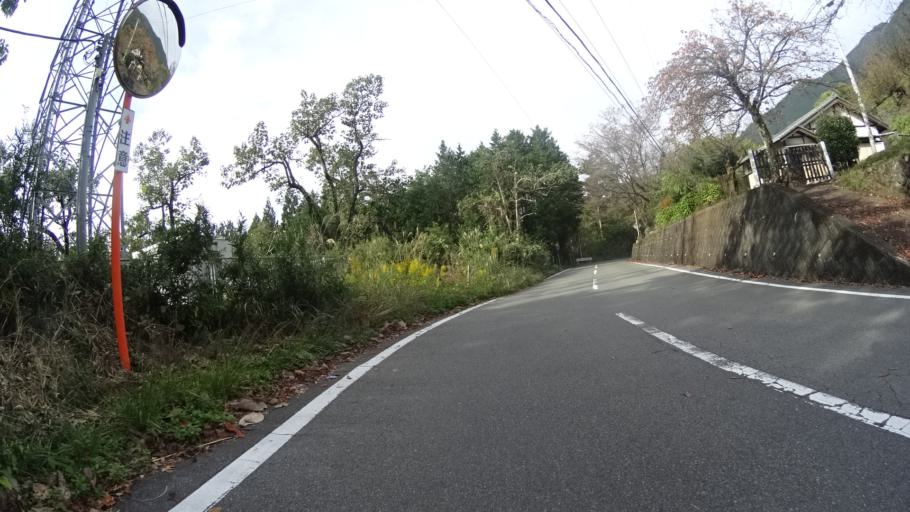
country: JP
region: Yamanashi
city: Uenohara
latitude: 35.6249
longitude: 139.0275
